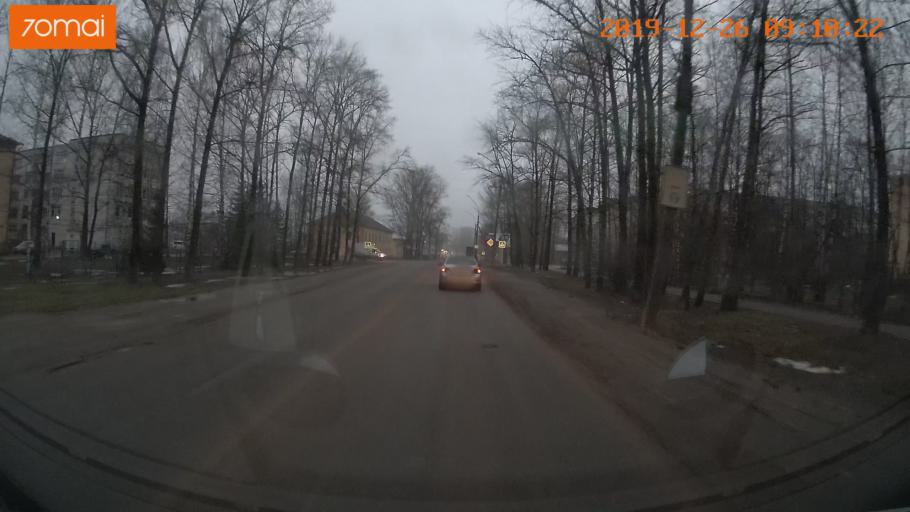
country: RU
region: Vologda
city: Gryazovets
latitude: 58.8705
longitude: 40.2527
